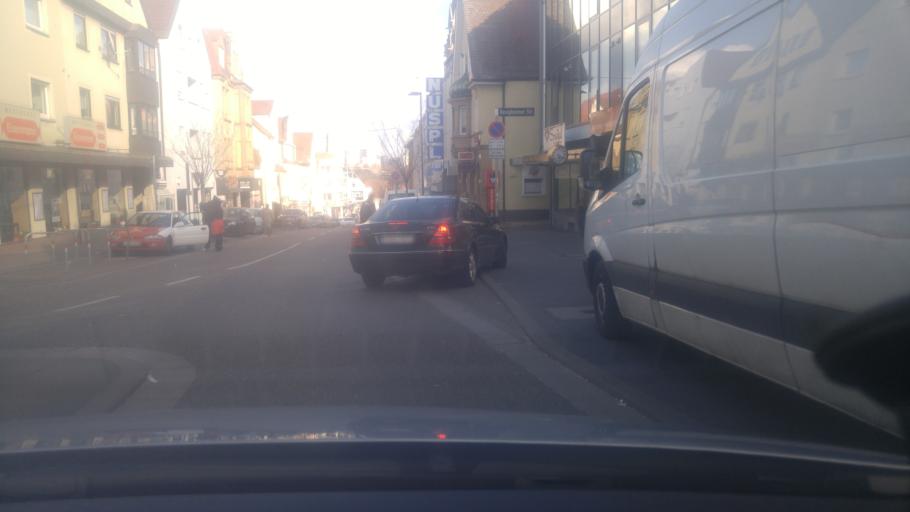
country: DE
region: Baden-Wuerttemberg
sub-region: Regierungsbezirk Stuttgart
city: Stuttgart Feuerbach
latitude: 48.8321
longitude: 9.1716
